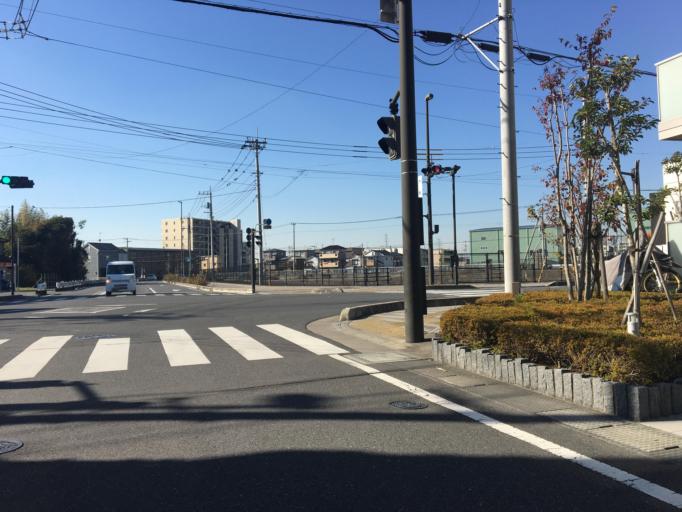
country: JP
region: Saitama
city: Yashio-shi
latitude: 35.8033
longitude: 139.8490
